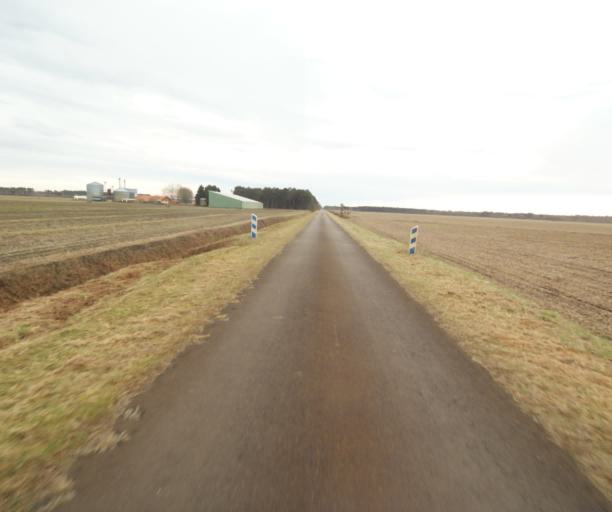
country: FR
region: Aquitaine
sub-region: Departement des Landes
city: Gabarret
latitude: 44.0372
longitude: -0.0718
